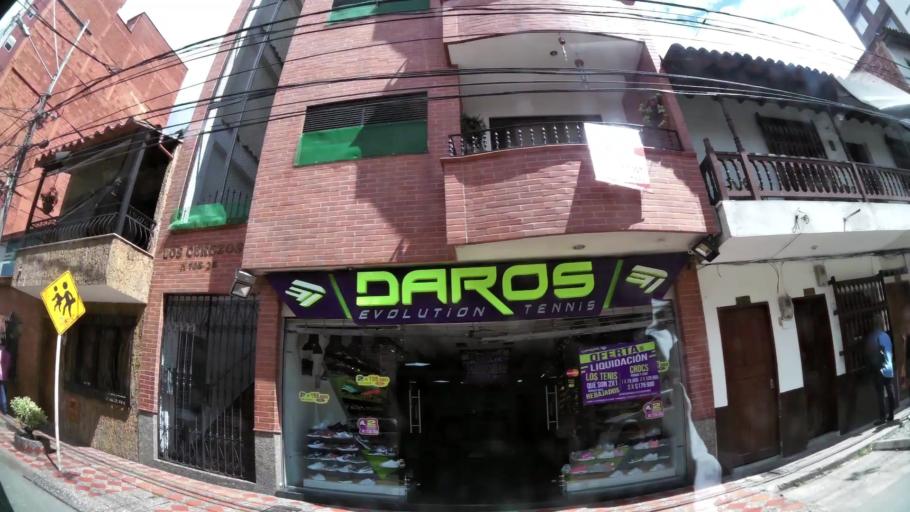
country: CO
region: Antioquia
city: Sabaneta
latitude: 6.1504
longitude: -75.6153
